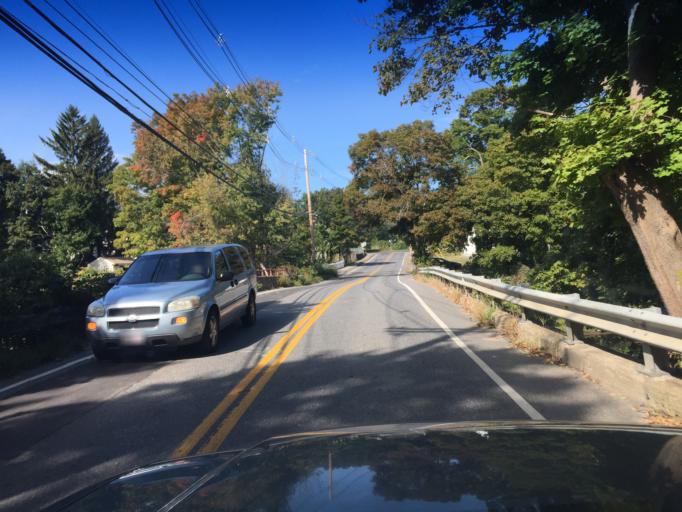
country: US
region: Massachusetts
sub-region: Middlesex County
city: Hudson
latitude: 42.3892
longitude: -71.5594
